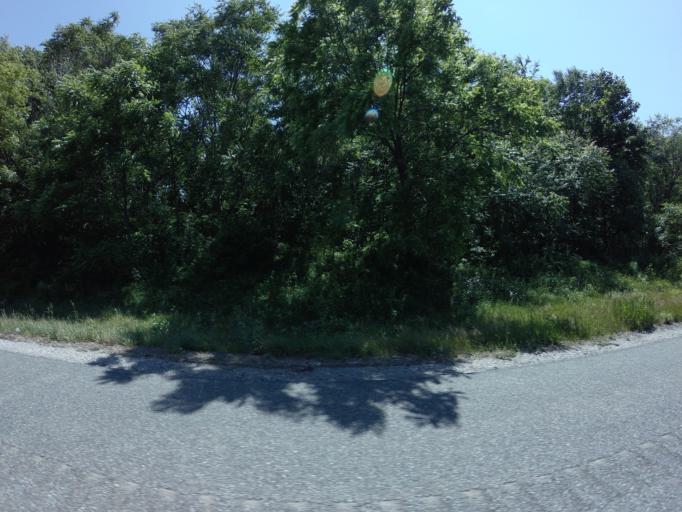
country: US
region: Maryland
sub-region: Carroll County
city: Mount Airy
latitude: 39.3506
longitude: -77.1110
